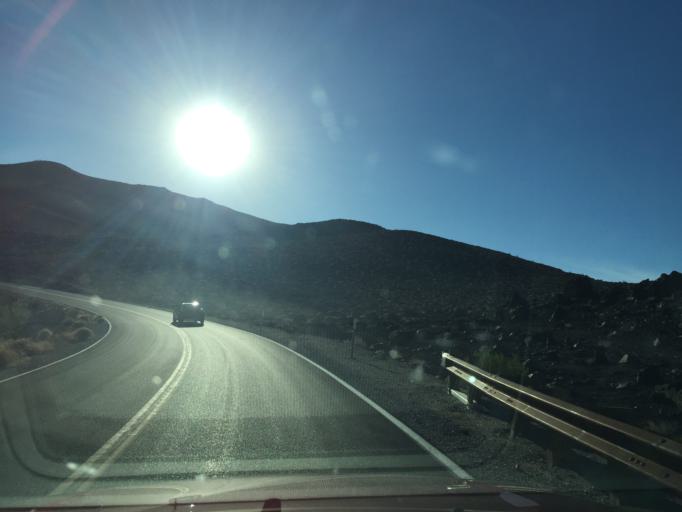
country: US
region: California
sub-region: Inyo County
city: Lone Pine
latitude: 36.3583
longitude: -117.5337
